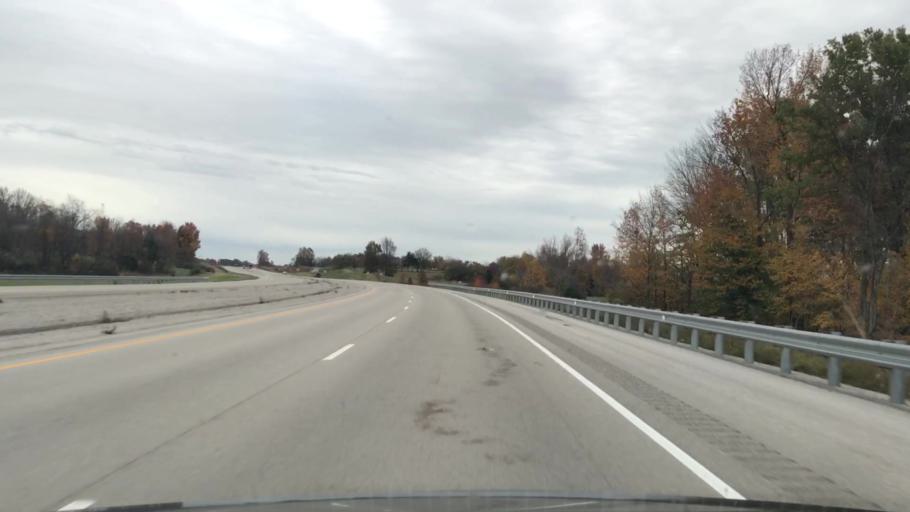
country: US
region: Kentucky
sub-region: Barren County
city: Glasgow
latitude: 37.0009
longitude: -85.9631
